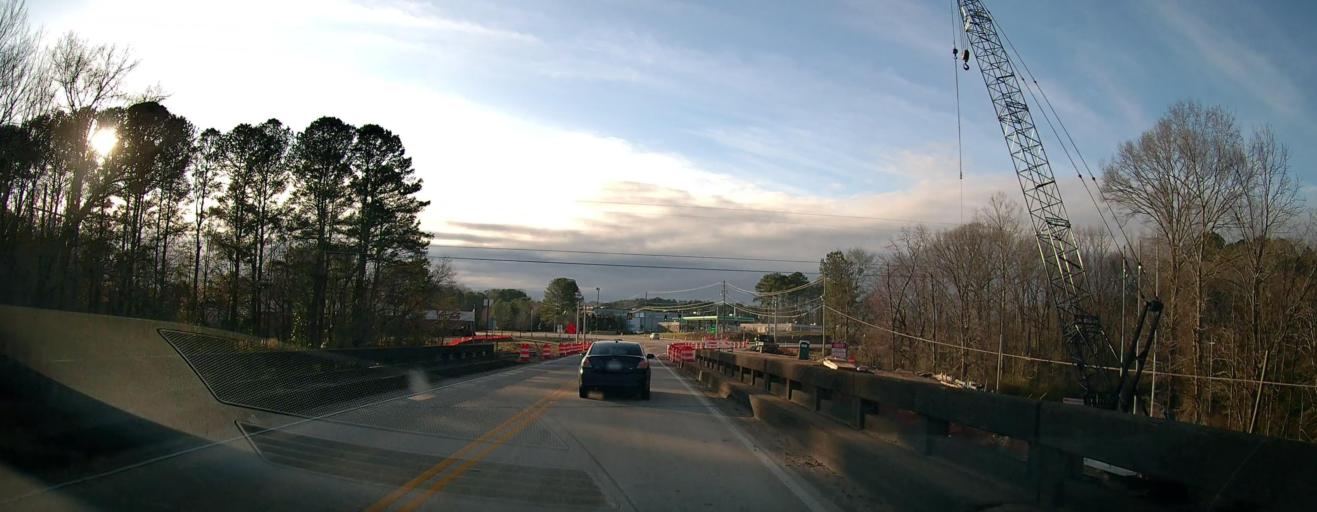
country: US
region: Georgia
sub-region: Troup County
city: West Point
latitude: 32.8785
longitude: -85.1535
